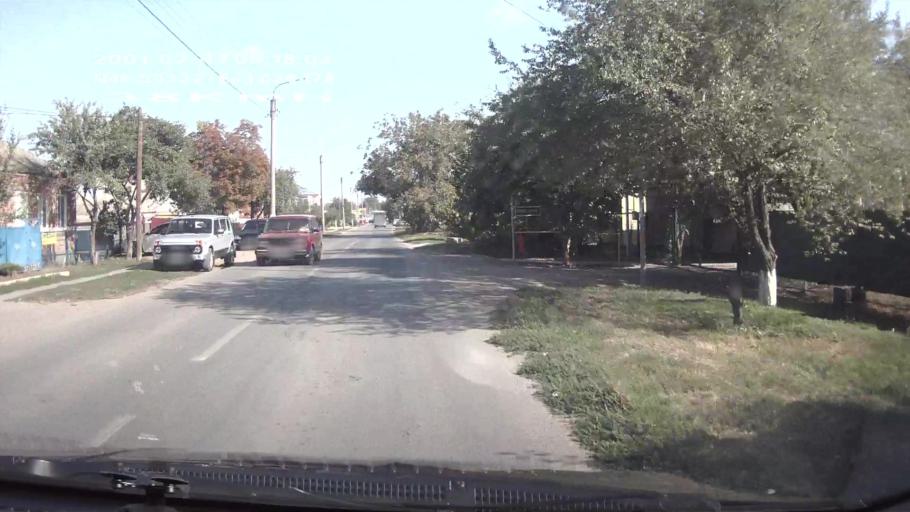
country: RU
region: Rostov
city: Tselina
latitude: 46.5334
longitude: 41.0265
